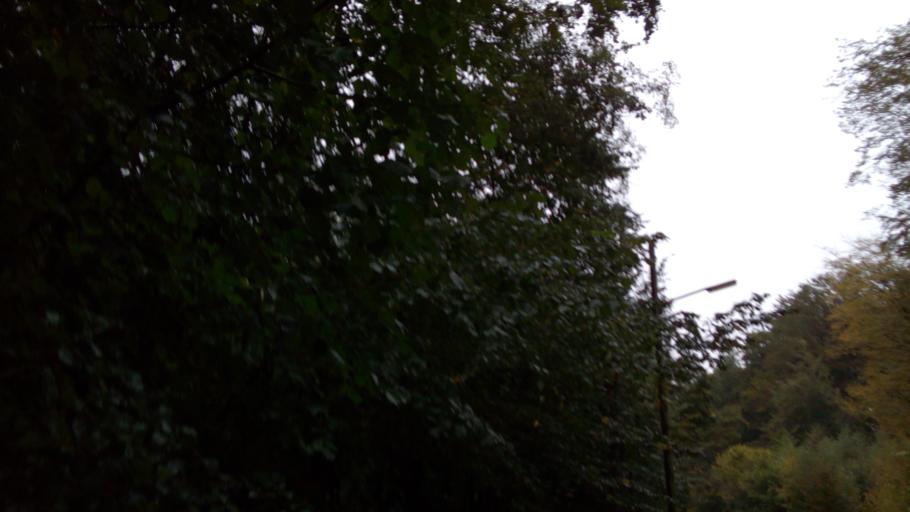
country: DE
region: North Rhine-Westphalia
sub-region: Regierungsbezirk Arnsberg
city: Bochum
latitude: 51.4398
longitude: 7.2760
